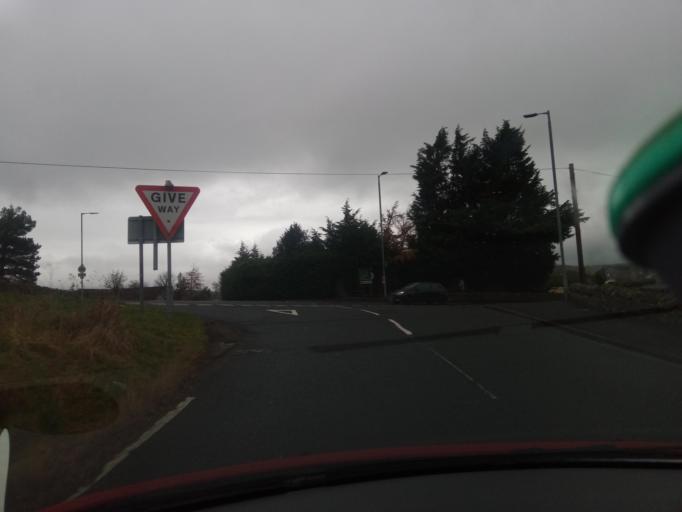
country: GB
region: Scotland
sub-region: The Scottish Borders
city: Selkirk
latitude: 55.5426
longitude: -2.8325
